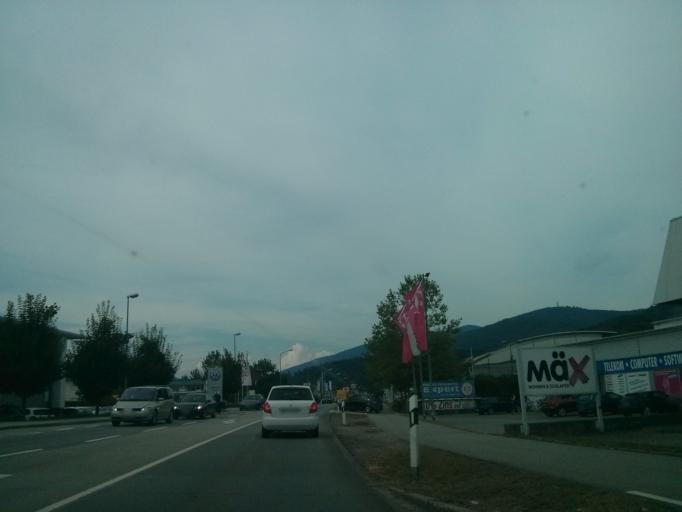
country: DE
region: Bavaria
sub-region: Lower Bavaria
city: Deggendorf
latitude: 48.8495
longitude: 12.9590
